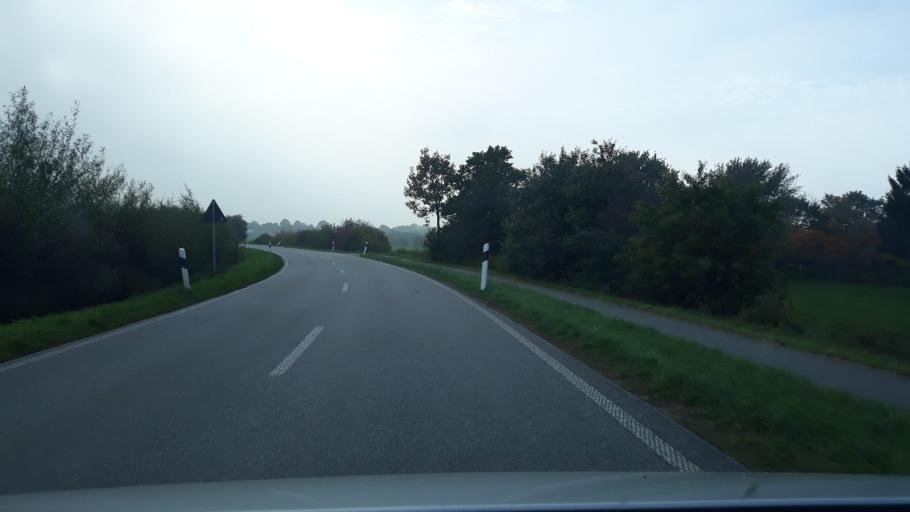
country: DE
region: Schleswig-Holstein
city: Klein Rheide
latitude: 54.4581
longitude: 9.4796
